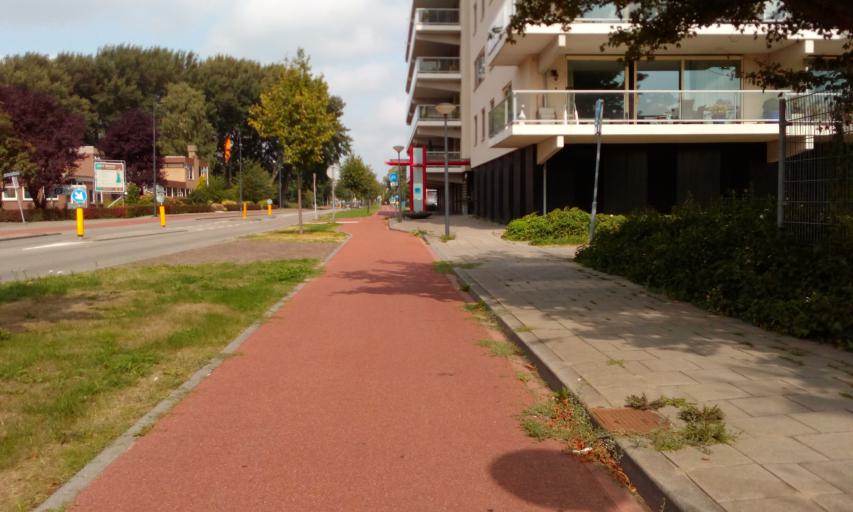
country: NL
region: South Holland
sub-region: Gemeente Vlaardingen
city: Vlaardingen
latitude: 51.9322
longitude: 4.3600
